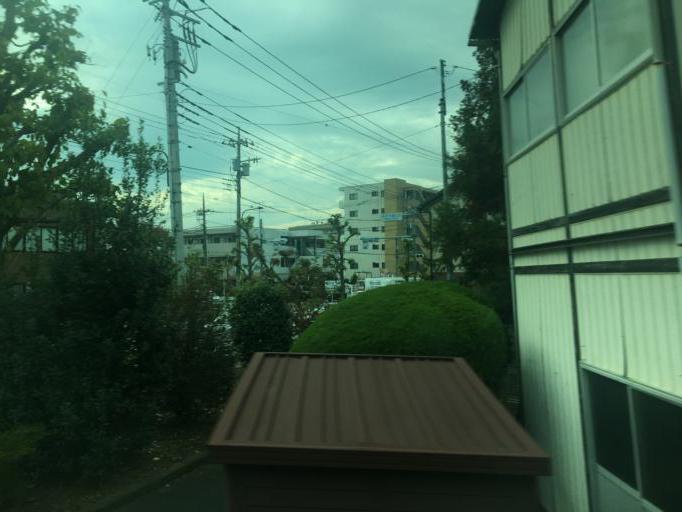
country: JP
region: Tokyo
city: Hino
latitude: 35.6917
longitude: 139.4245
